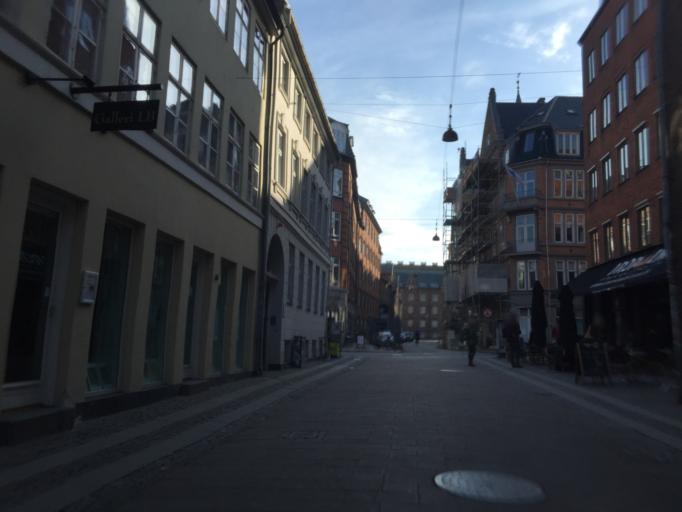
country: DK
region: Capital Region
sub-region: Kobenhavn
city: Copenhagen
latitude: 55.6765
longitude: 12.5739
